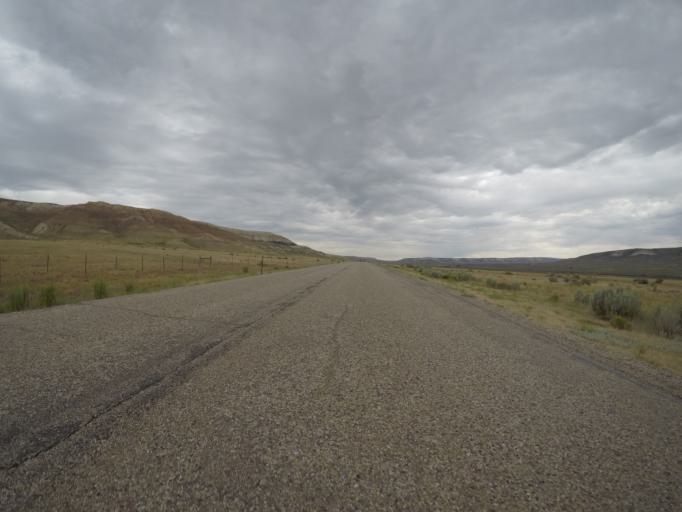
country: US
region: Wyoming
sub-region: Lincoln County
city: Kemmerer
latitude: 41.8230
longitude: -110.7495
